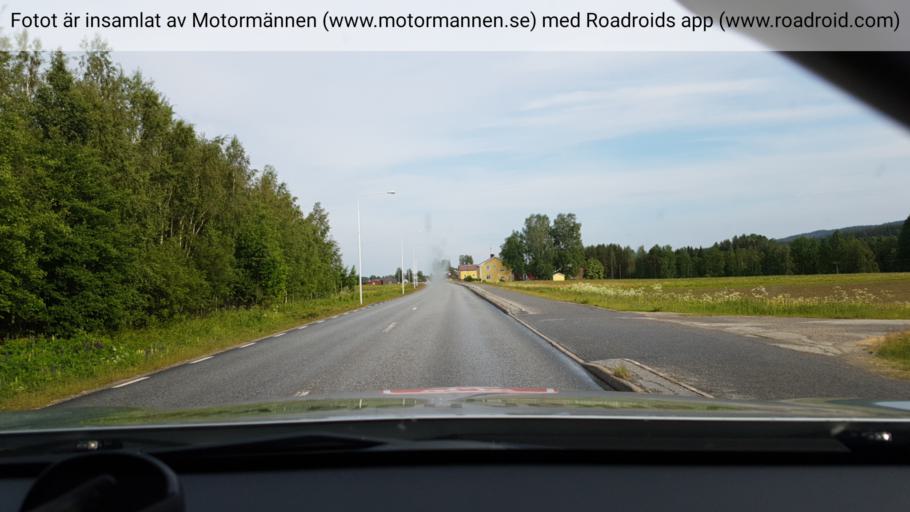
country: SE
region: Vaesterbotten
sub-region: Bjurholms Kommun
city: Bjurholm
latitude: 64.2609
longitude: 19.2835
